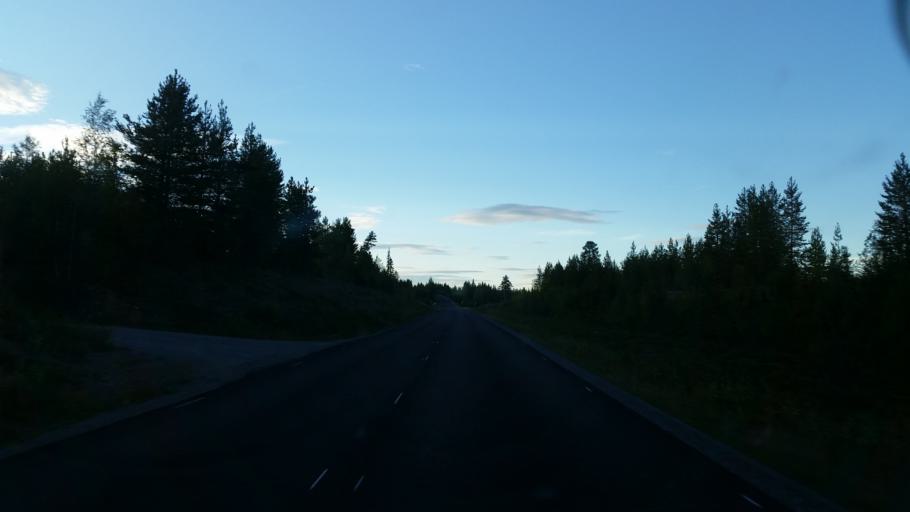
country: SE
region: Vaesterbotten
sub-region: Vilhelmina Kommun
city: Vilhelmina
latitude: 64.7333
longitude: 16.7094
